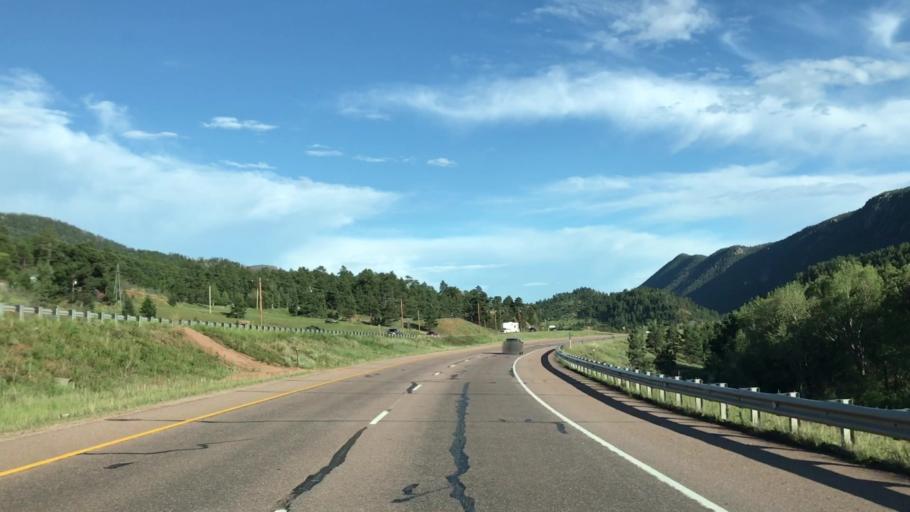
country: US
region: Colorado
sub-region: El Paso County
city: Cascade-Chipita Park
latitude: 38.9475
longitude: -105.0227
